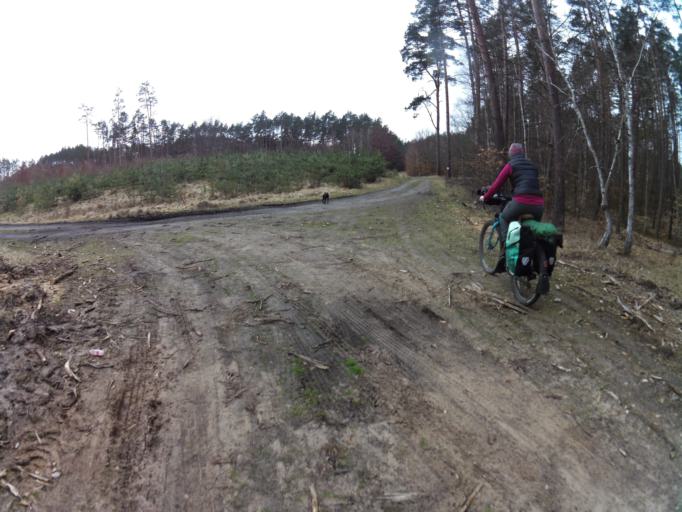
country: PL
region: West Pomeranian Voivodeship
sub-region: Powiat mysliborski
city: Debno
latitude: 52.7674
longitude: 14.8168
